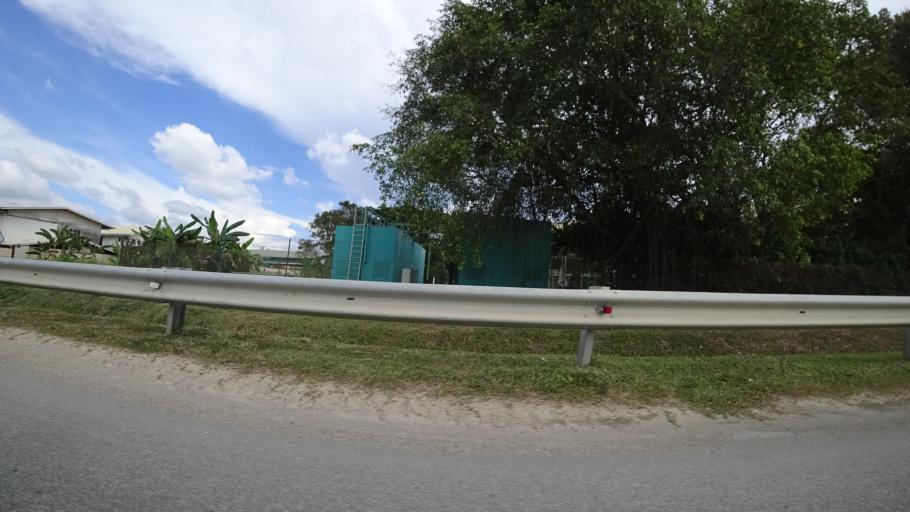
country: BN
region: Brunei and Muara
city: Bandar Seri Begawan
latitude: 4.8427
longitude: 114.8739
